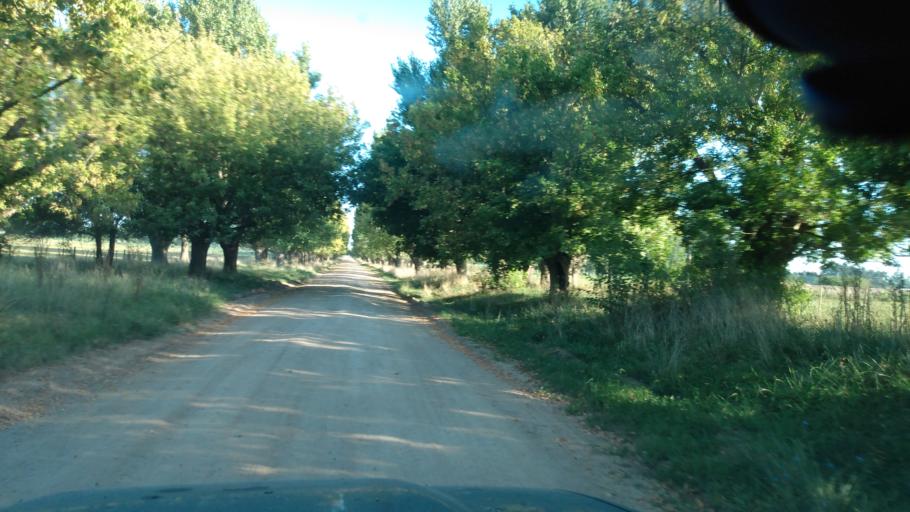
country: AR
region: Buenos Aires
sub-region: Partido de Lujan
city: Lujan
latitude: -34.5897
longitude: -59.0732
